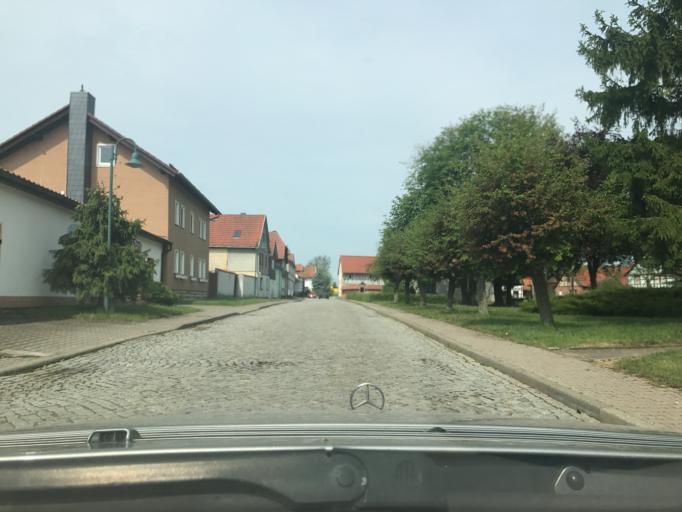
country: DE
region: Thuringia
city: Menteroda
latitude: 51.2638
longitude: 10.5270
